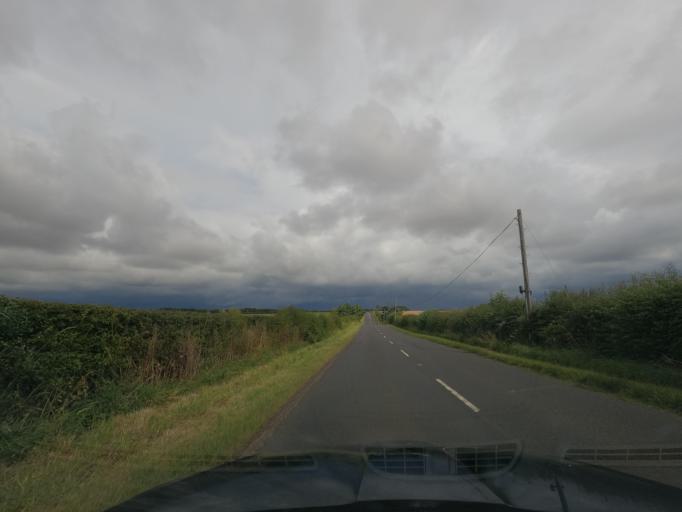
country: GB
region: England
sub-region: Northumberland
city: Ancroft
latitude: 55.6926
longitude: -1.9999
